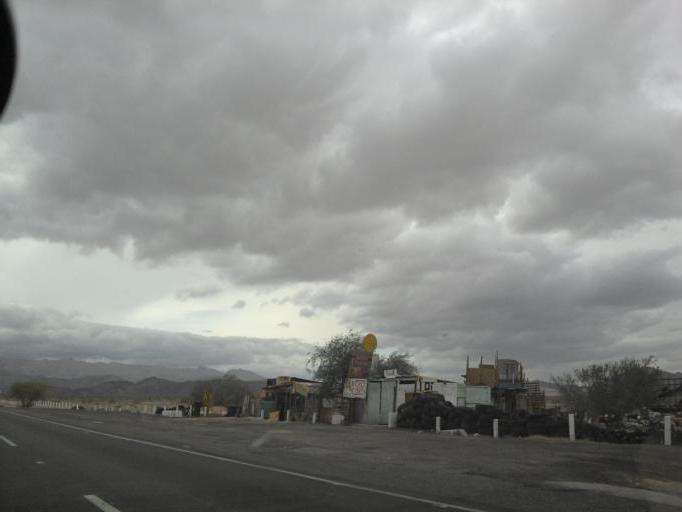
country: US
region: California
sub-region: Imperial County
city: Seeley
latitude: 32.5651
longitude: -115.8883
